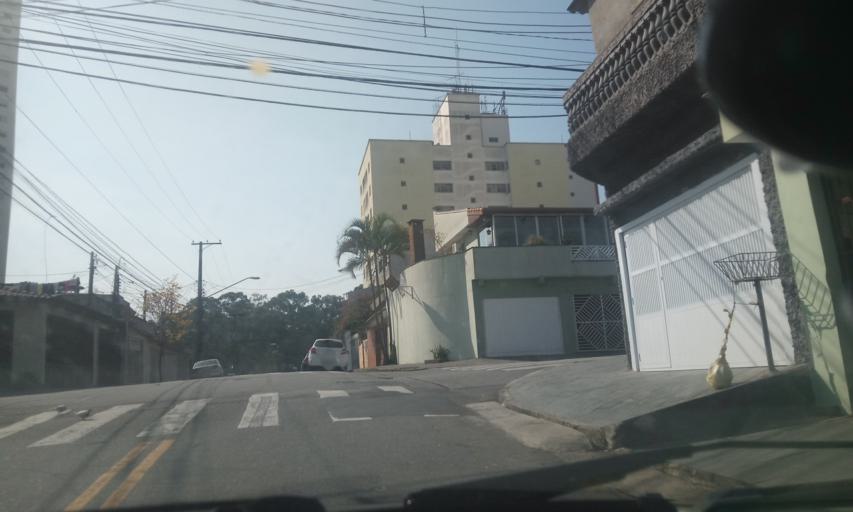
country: BR
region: Sao Paulo
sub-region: Sao Bernardo Do Campo
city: Sao Bernardo do Campo
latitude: -23.7109
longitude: -46.5574
